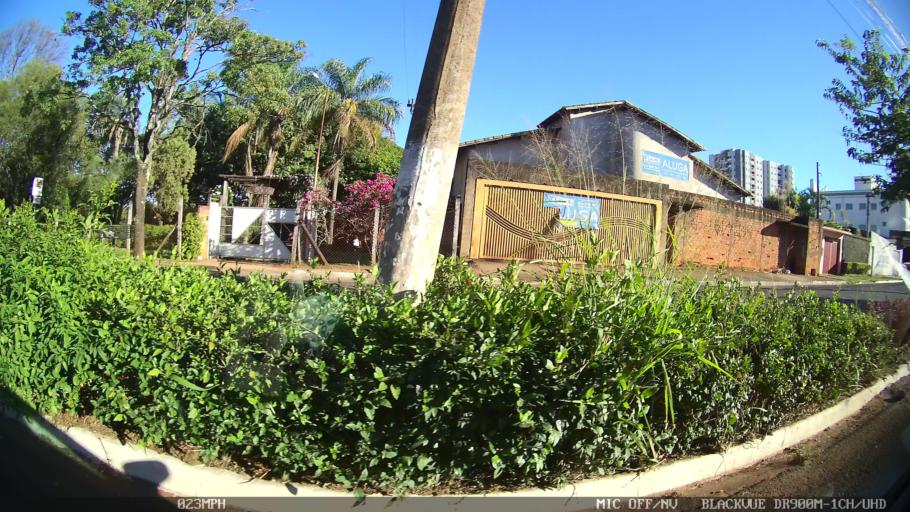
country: BR
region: Sao Paulo
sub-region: Franca
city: Franca
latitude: -20.5658
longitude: -47.4036
